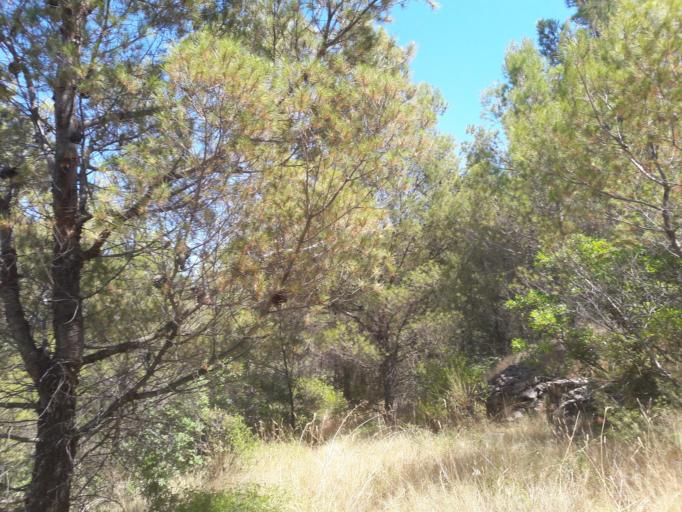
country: HR
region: Sibensko-Kniniska
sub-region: Grad Sibenik
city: Sibenik
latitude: 43.6911
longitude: 15.8556
